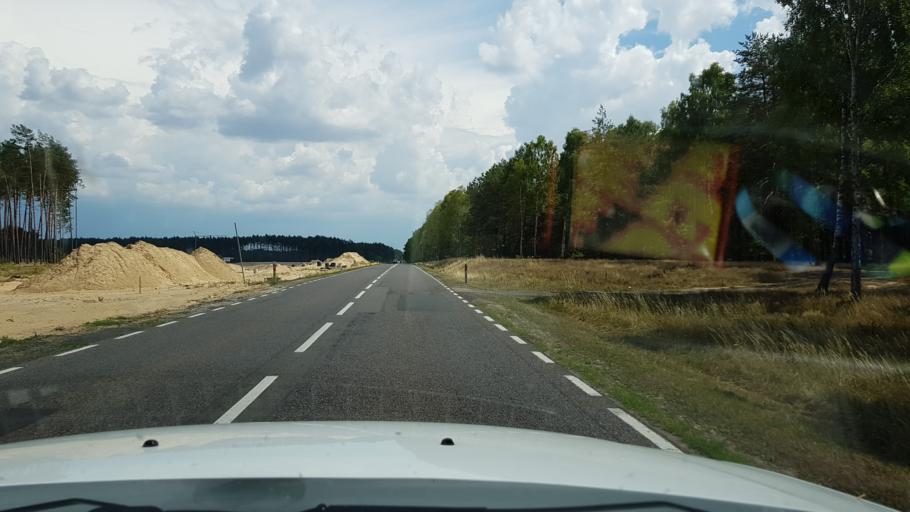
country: PL
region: West Pomeranian Voivodeship
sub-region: Powiat walecki
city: Walcz
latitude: 53.2983
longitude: 16.4179
